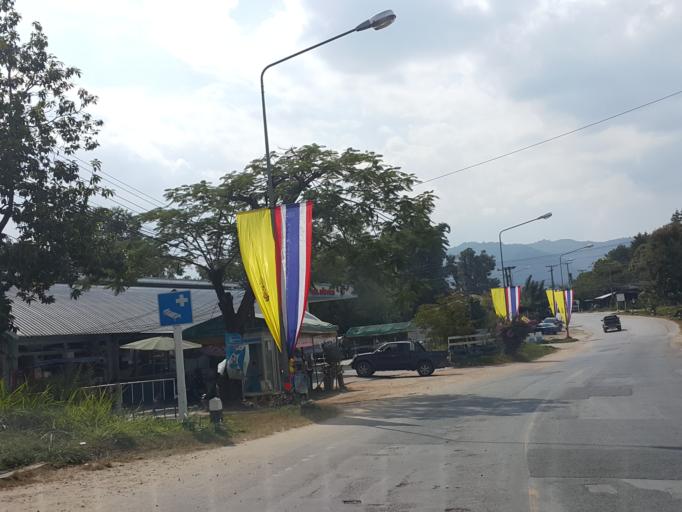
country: TH
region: Chiang Mai
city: Om Koi
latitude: 17.8021
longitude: 98.3623
